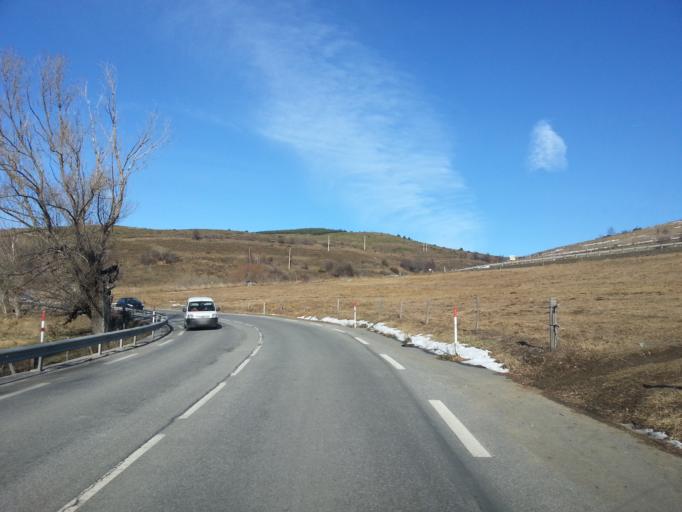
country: ES
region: Catalonia
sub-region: Provincia de Girona
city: Llivia
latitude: 42.4689
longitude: 2.0354
